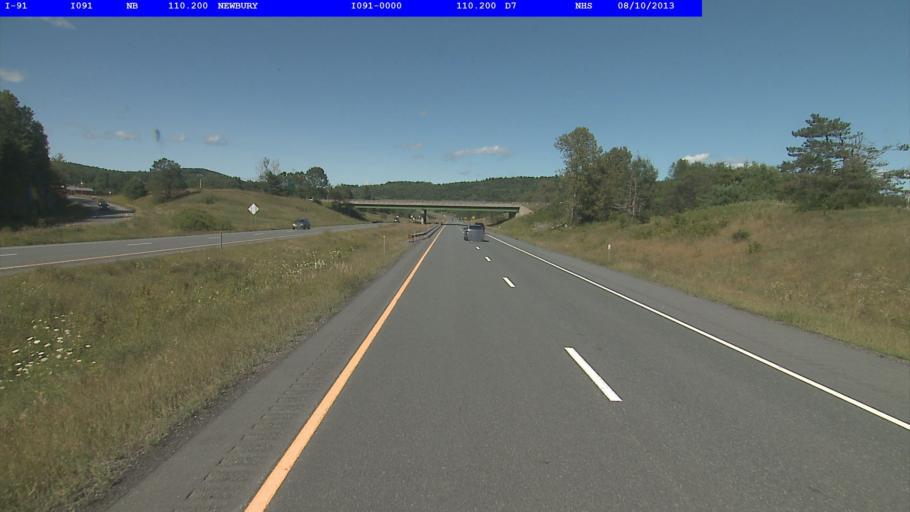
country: US
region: New Hampshire
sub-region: Grafton County
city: Woodsville
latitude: 44.1583
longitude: -72.0899
